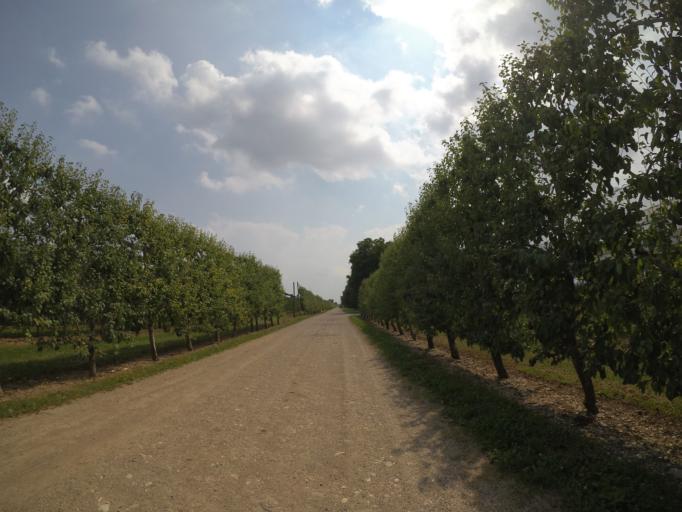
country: IT
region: Friuli Venezia Giulia
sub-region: Provincia di Udine
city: Sedegliano
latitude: 45.9937
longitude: 13.0108
